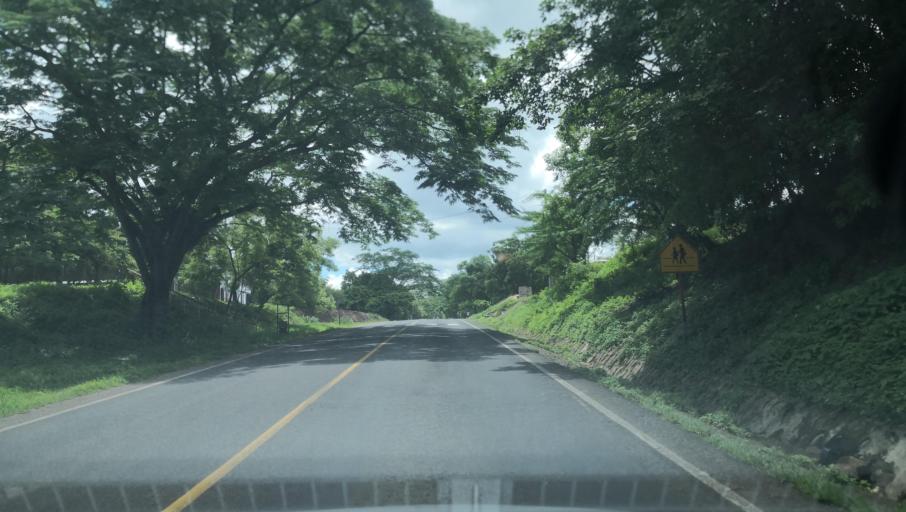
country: NI
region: Madriz
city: Palacaguina
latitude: 13.4202
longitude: -86.4003
